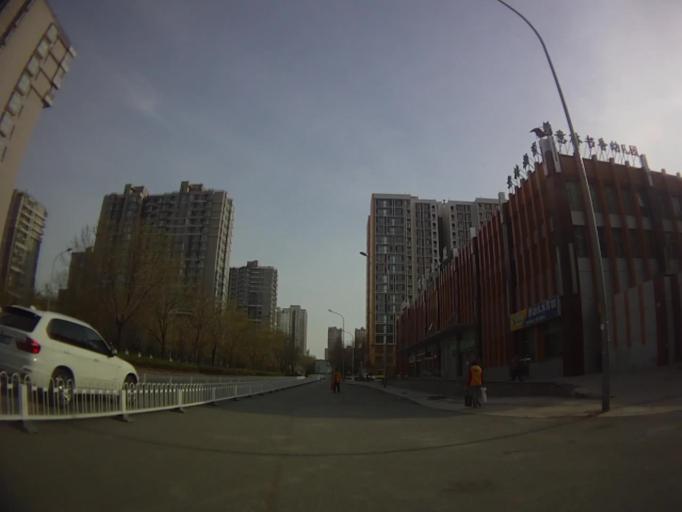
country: CN
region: Beijing
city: Longtan
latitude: 39.8958
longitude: 116.4441
